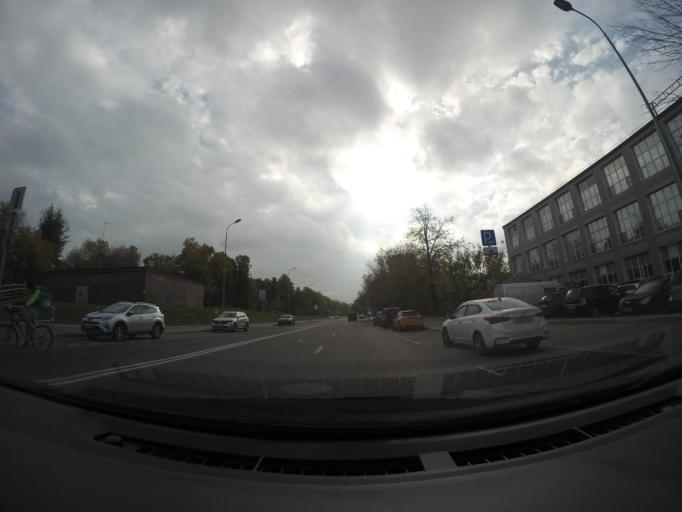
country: RU
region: Moscow
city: Lefortovo
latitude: 55.7802
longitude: 37.7167
